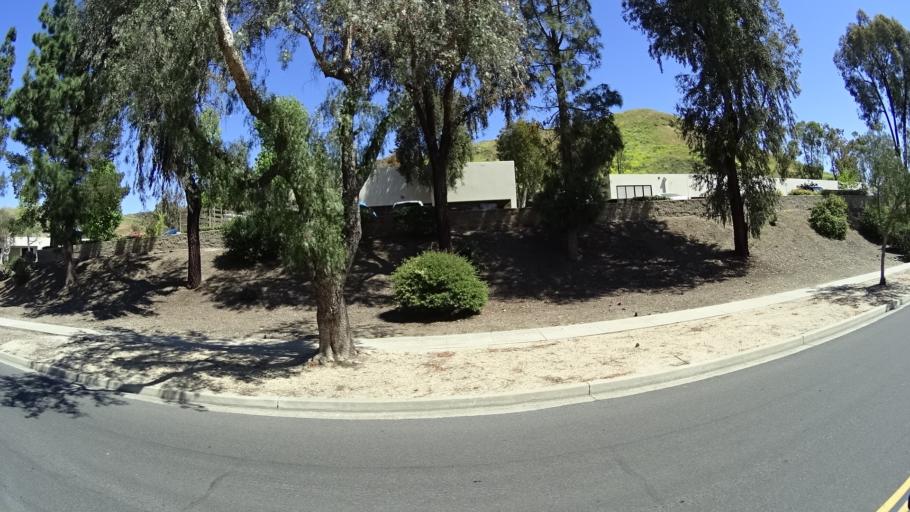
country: US
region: California
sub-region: Ventura County
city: Casa Conejo
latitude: 34.1925
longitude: -118.9562
